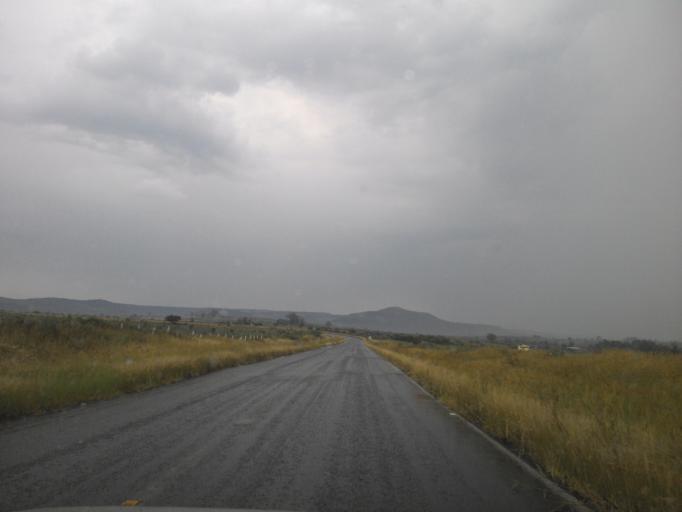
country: MX
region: Jalisco
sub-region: Arandas
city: Santiaguito (Santiaguito de Velazquez)
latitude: 20.8385
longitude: -102.1051
